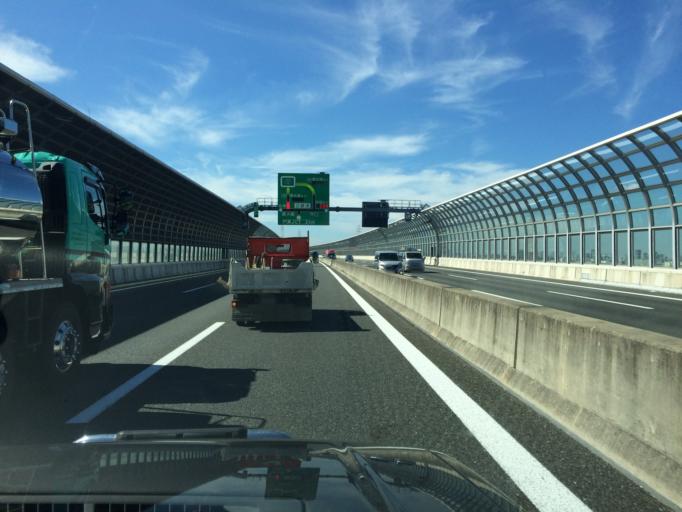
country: JP
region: Osaka
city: Daitocho
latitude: 34.7312
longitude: 135.6065
